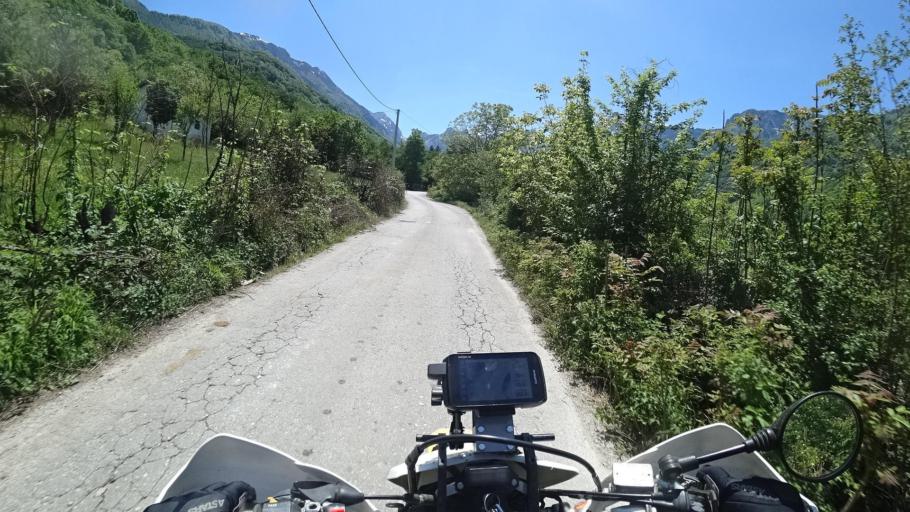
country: BA
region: Federation of Bosnia and Herzegovina
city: Bijela
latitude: 43.6108
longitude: 17.9549
